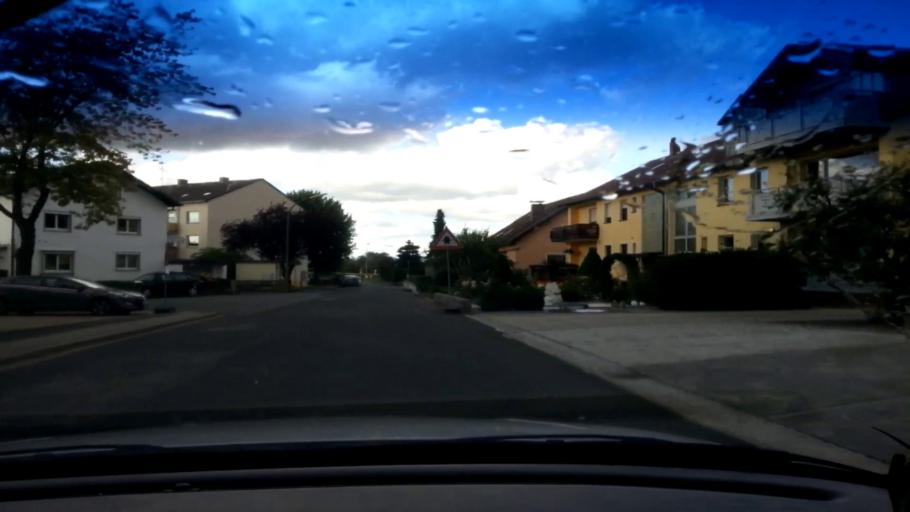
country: DE
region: Bavaria
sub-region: Upper Franconia
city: Zapfendorf
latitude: 50.0219
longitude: 10.9382
